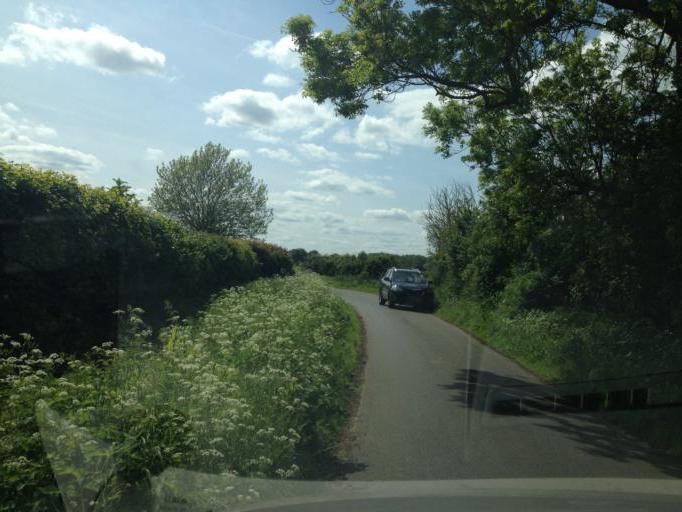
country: GB
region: England
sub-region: Oxfordshire
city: Wheatley
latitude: 51.7459
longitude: -1.0682
